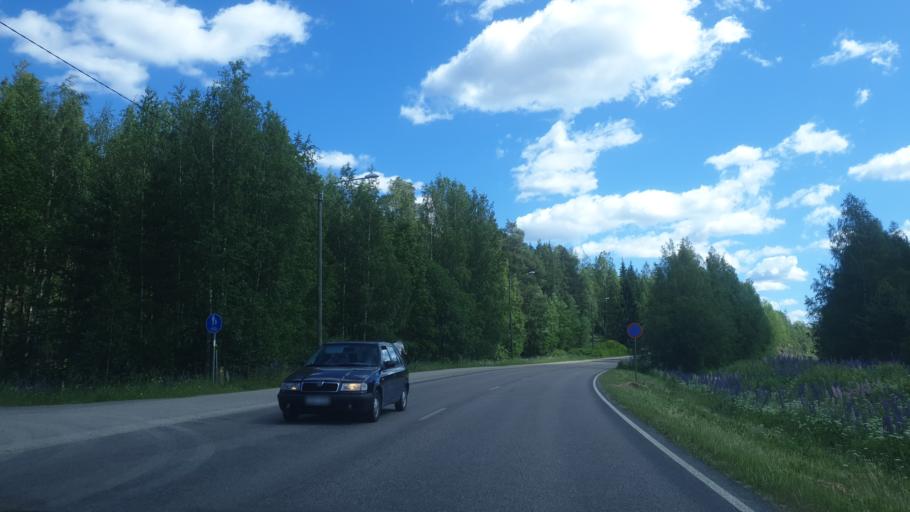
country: FI
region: Northern Savo
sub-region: Varkaus
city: Varkaus
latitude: 62.3376
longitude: 27.8551
